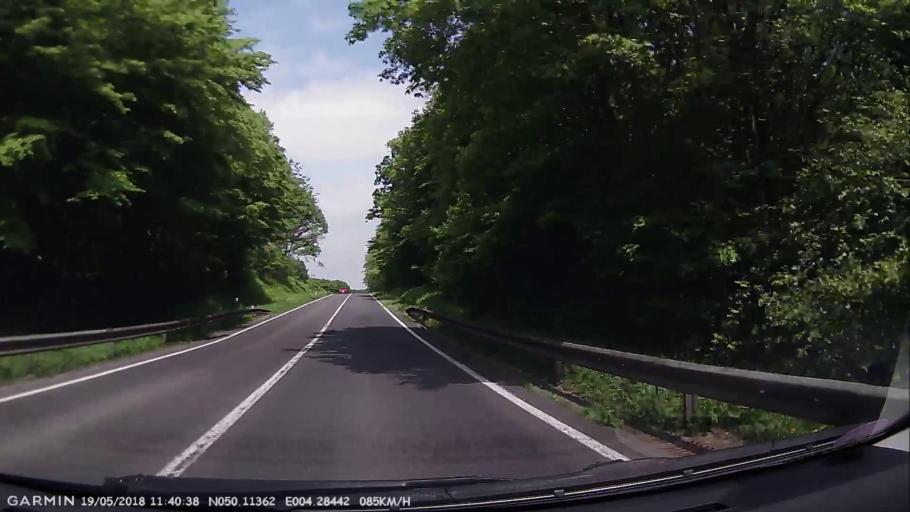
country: BE
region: Wallonia
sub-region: Province du Hainaut
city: Froidchapelle
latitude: 50.1139
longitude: 4.2843
